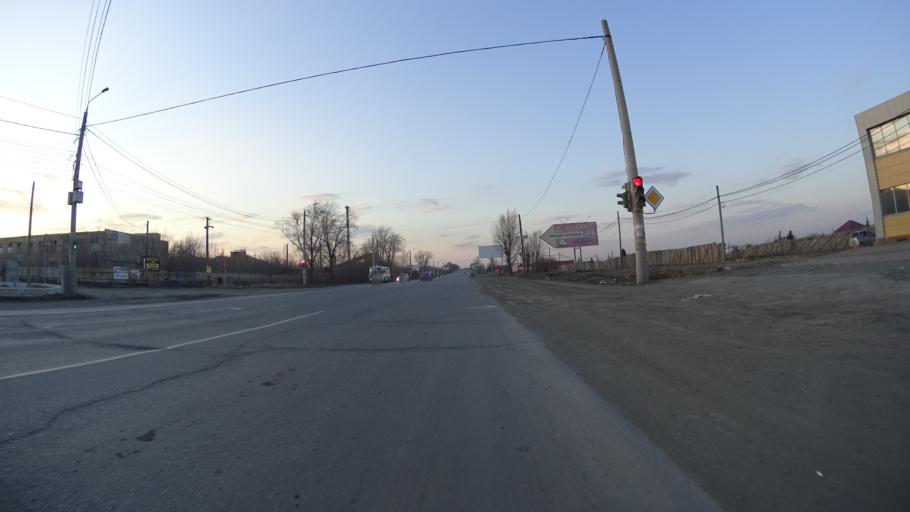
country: RU
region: Chelyabinsk
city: Novosineglazovskiy
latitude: 55.0948
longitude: 61.3881
